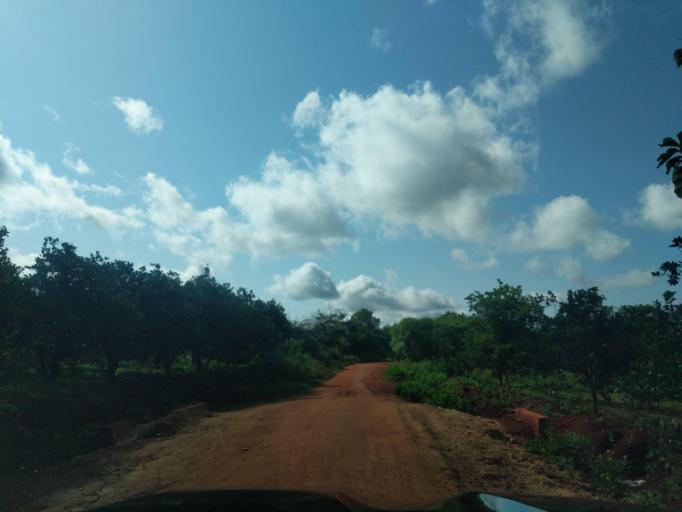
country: TZ
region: Tanga
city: Muheza
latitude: -5.4193
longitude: 38.6282
